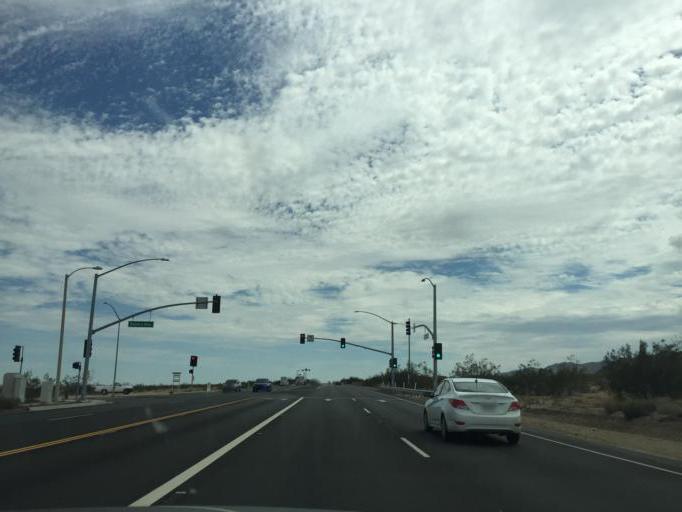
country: US
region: California
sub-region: San Bernardino County
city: Joshua Tree
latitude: 34.1351
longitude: -116.2130
